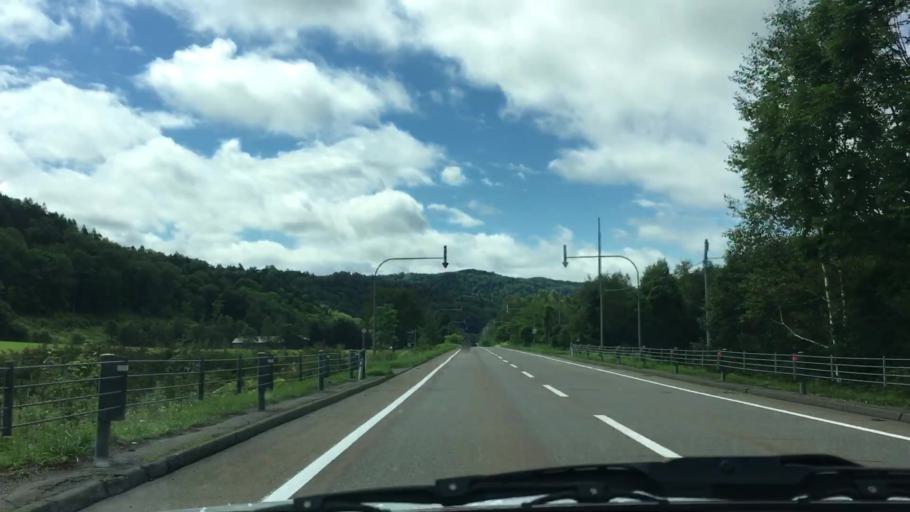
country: JP
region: Hokkaido
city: Kitami
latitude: 43.3915
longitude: 143.9214
